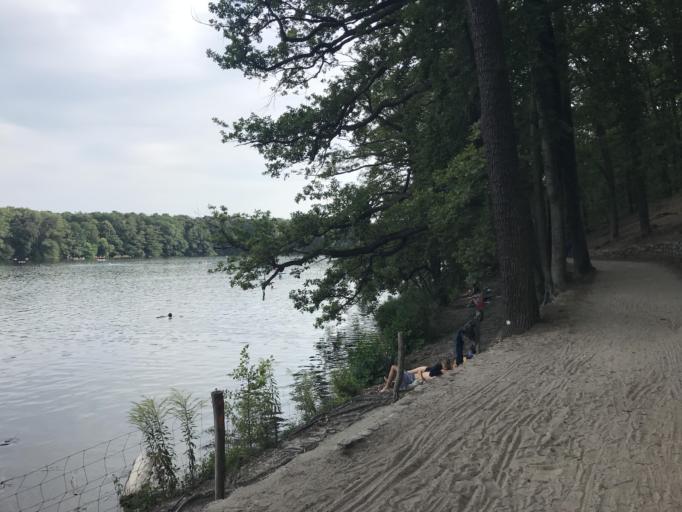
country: DE
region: Berlin
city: Nikolassee
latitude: 52.4453
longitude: 13.2168
